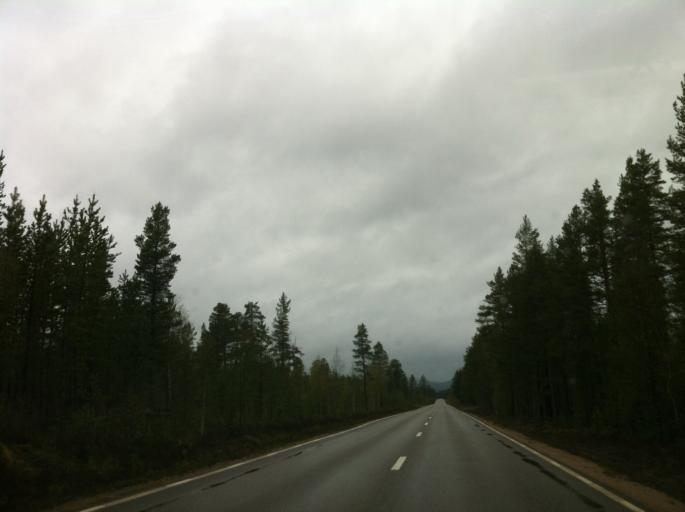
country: SE
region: Jaemtland
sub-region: Harjedalens Kommun
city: Sveg
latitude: 62.1366
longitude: 13.9973
